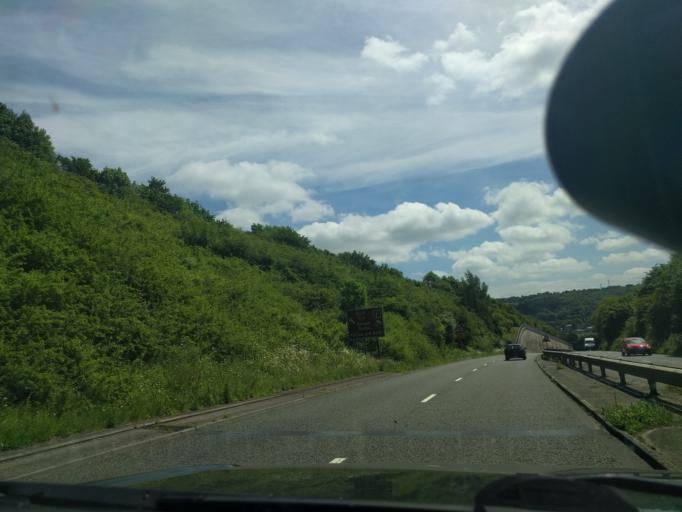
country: GB
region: England
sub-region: Bath and North East Somerset
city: Bath
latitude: 51.4061
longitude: -2.3404
